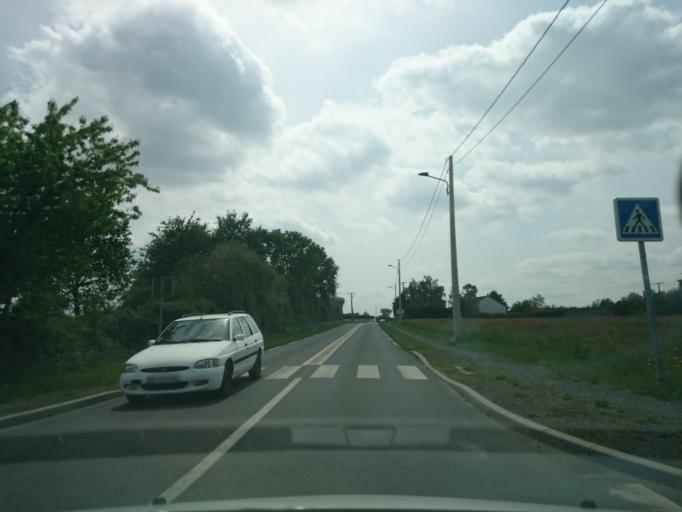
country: FR
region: Pays de la Loire
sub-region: Departement de la Loire-Atlantique
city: Pont-Saint-Martin
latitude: 47.1086
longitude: -1.5874
